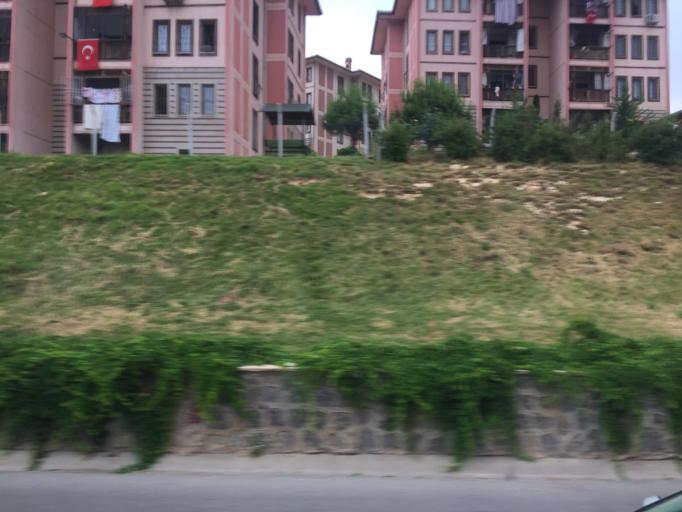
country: TR
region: Gaziantep
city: Gaziantep
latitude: 37.0430
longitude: 37.4246
